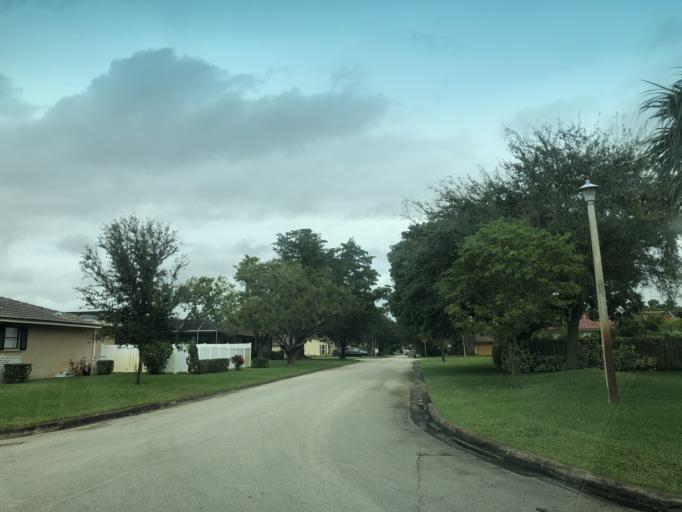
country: US
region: Florida
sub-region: Broward County
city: North Lauderdale
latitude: 26.2420
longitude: -80.2400
